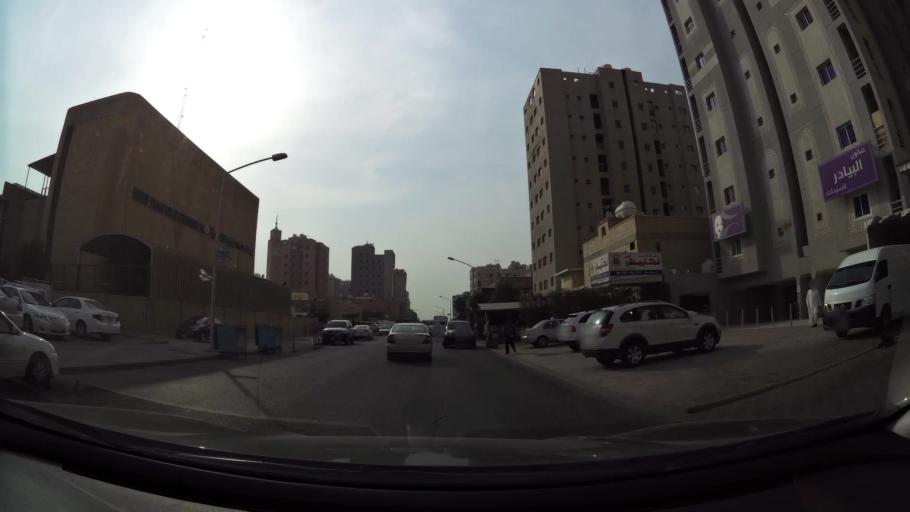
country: KW
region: Al Farwaniyah
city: Al Farwaniyah
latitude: 29.2952
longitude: 47.9710
